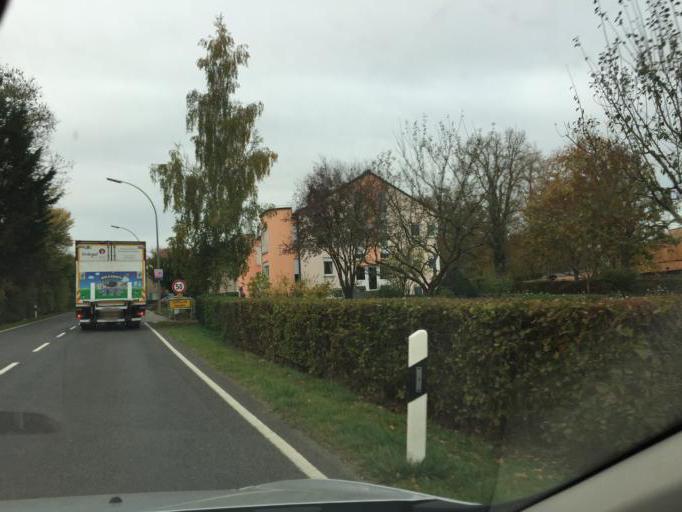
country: LU
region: Luxembourg
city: Capellen
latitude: 49.6476
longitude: 5.9871
